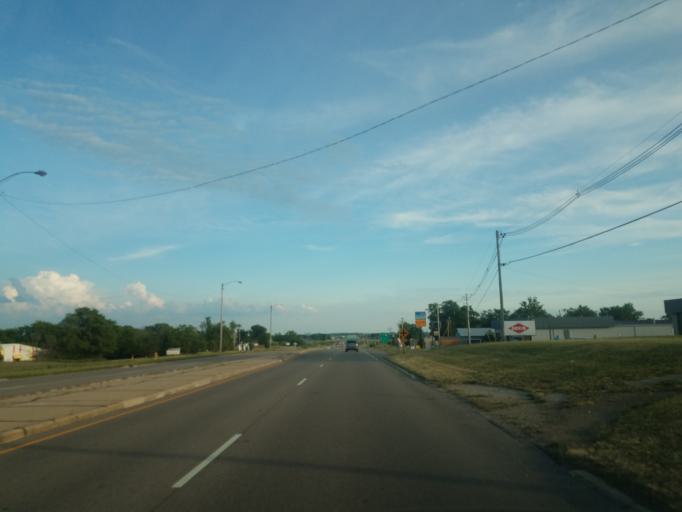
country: US
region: Illinois
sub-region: McLean County
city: Bloomington
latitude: 40.4433
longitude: -88.9912
